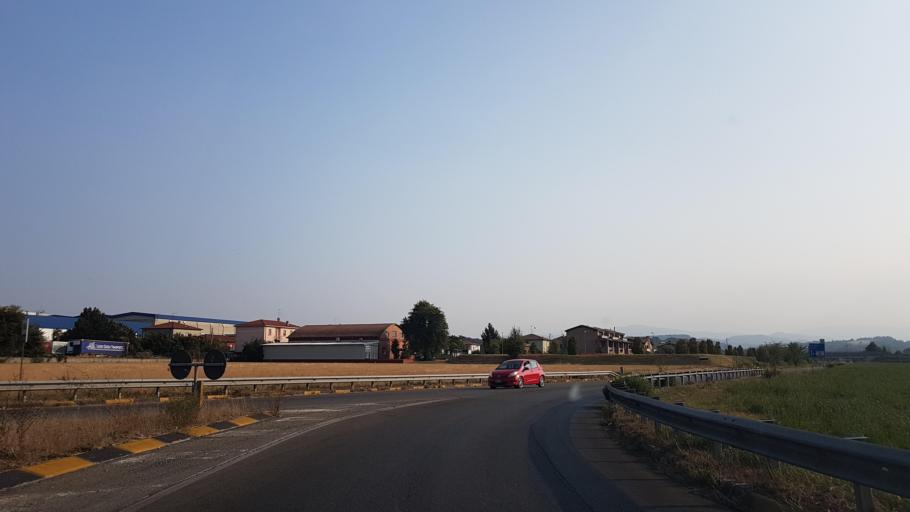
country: IT
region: Emilia-Romagna
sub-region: Provincia di Parma
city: Collecchio
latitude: 44.7586
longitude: 10.2032
